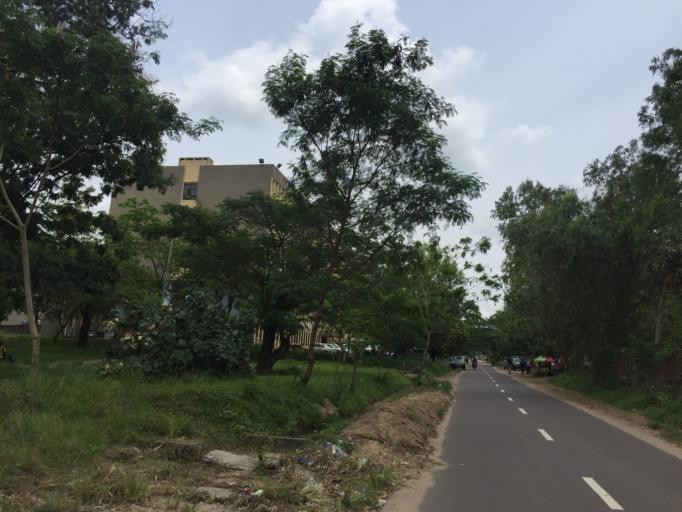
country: CD
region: Kinshasa
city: Kinshasa
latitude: -4.4169
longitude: 15.3060
